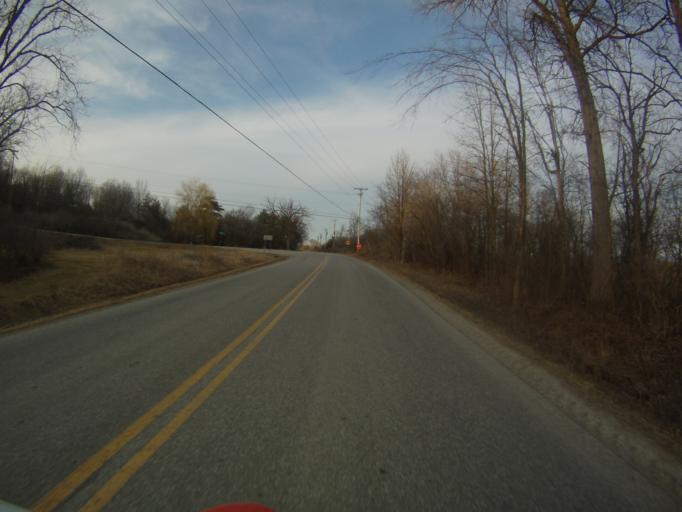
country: US
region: Vermont
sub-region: Addison County
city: Vergennes
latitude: 44.1401
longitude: -73.3446
